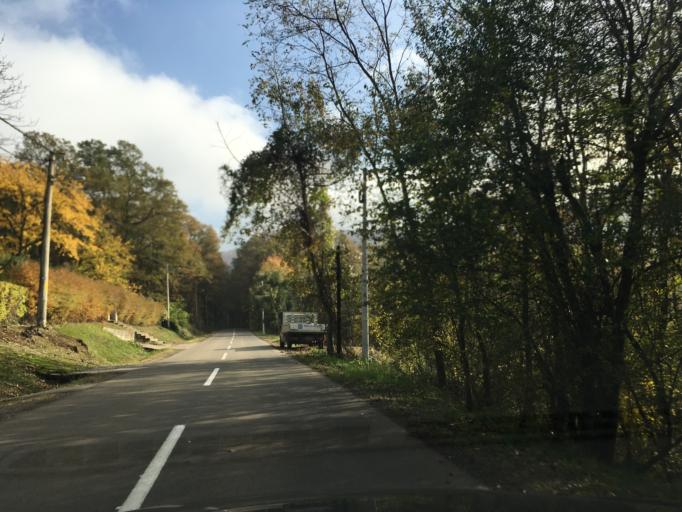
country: RS
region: Central Serbia
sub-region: Belgrade
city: Sopot
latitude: 44.4767
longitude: 20.5650
